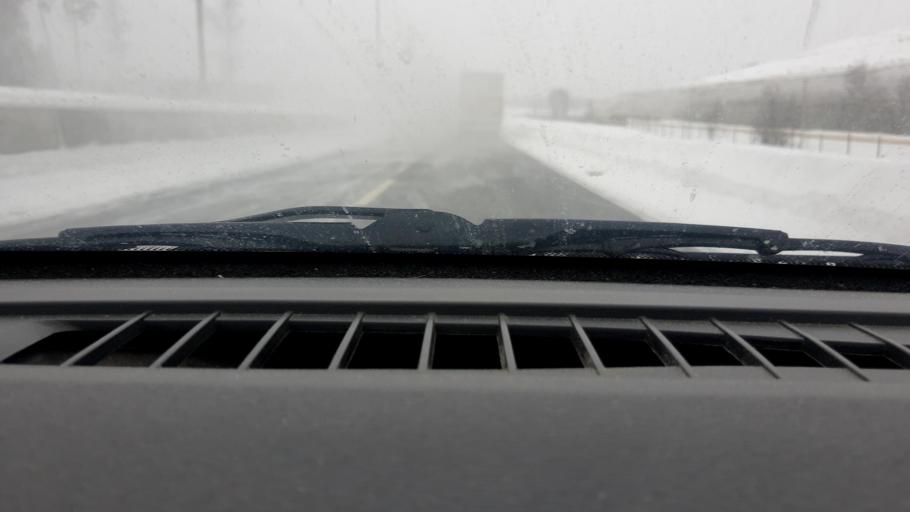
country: RU
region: Moskovskaya
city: Krasnoarmeysk
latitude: 56.0675
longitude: 38.0907
